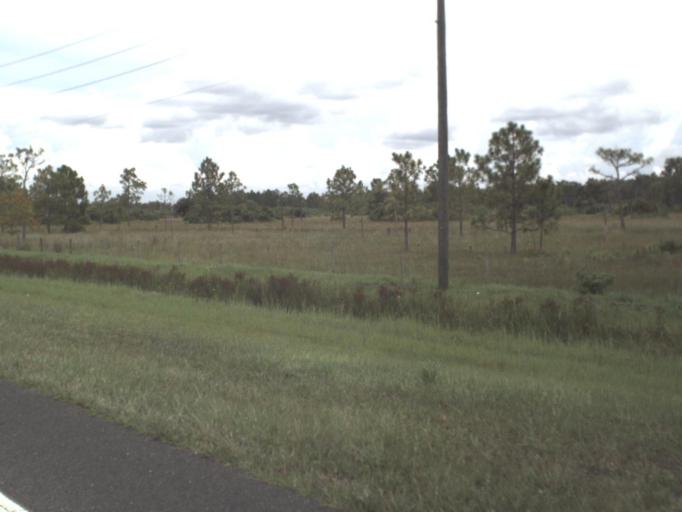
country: US
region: Florida
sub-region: Hillsborough County
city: Cheval
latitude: 28.1946
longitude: -82.5108
